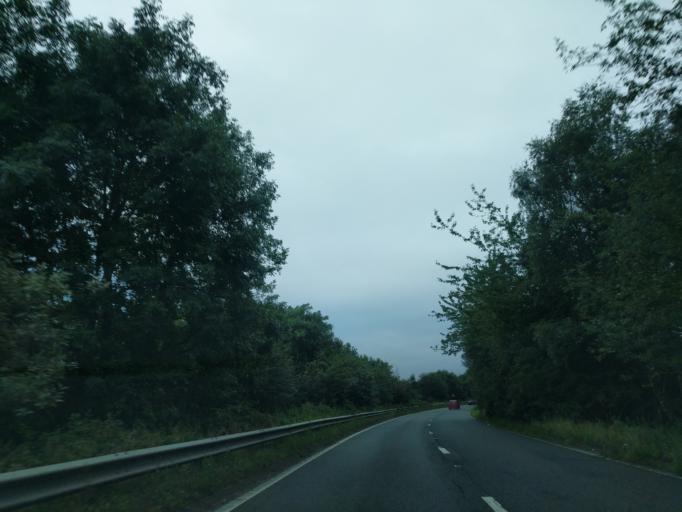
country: GB
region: England
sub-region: City and Borough of Birmingham
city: Bartley Green
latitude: 52.4515
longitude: -2.0077
